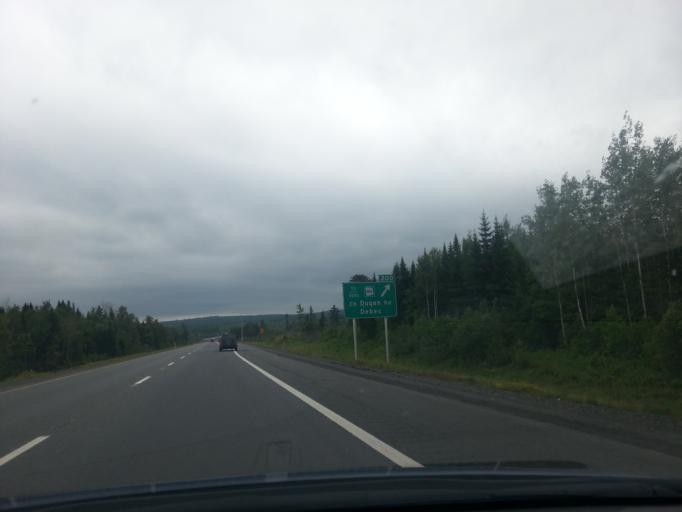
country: US
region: Maine
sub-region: Aroostook County
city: Houlton
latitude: 46.0485
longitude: -67.5648
